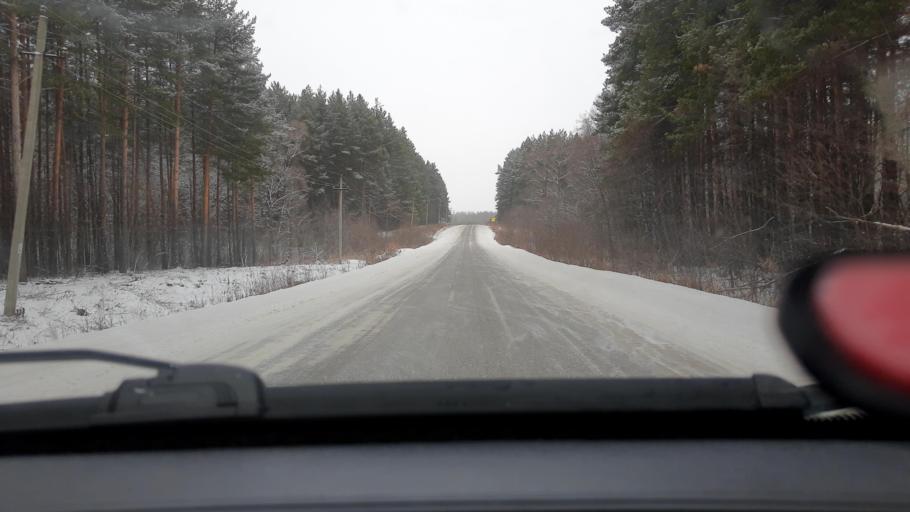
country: RU
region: Bashkortostan
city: Iglino
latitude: 54.6752
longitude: 56.4190
